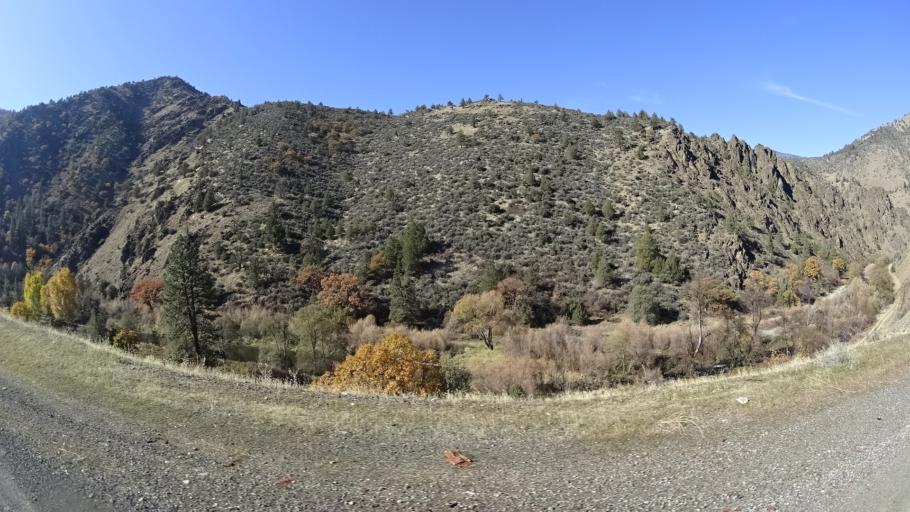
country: US
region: California
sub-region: Siskiyou County
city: Yreka
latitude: 41.8246
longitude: -122.5927
